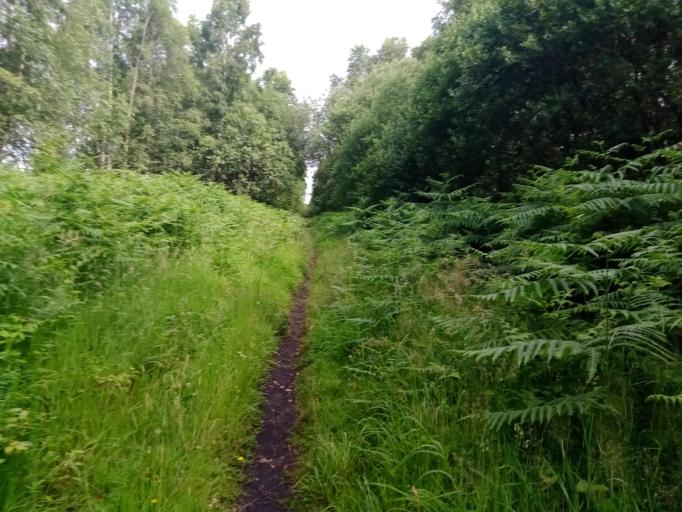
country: IE
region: Leinster
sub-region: Laois
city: Abbeyleix
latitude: 52.8841
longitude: -7.3504
